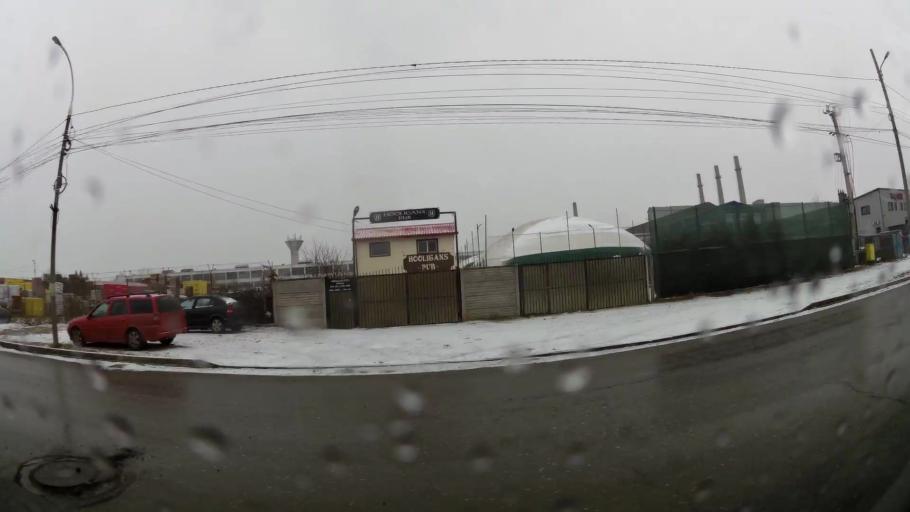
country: RO
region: Dambovita
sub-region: Municipiul Targoviste
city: Targoviste
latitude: 44.9264
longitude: 25.4324
